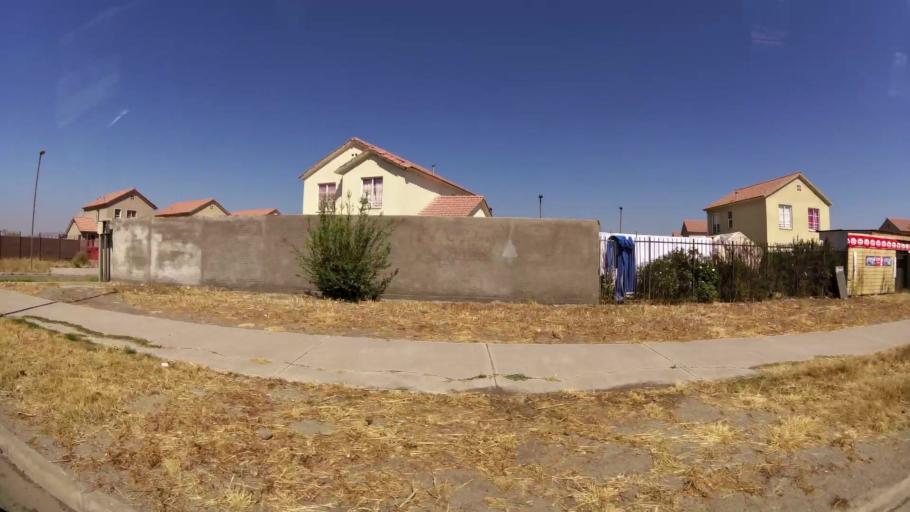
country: CL
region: Santiago Metropolitan
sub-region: Provincia de Chacabuco
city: Chicureo Abajo
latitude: -33.3269
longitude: -70.7400
